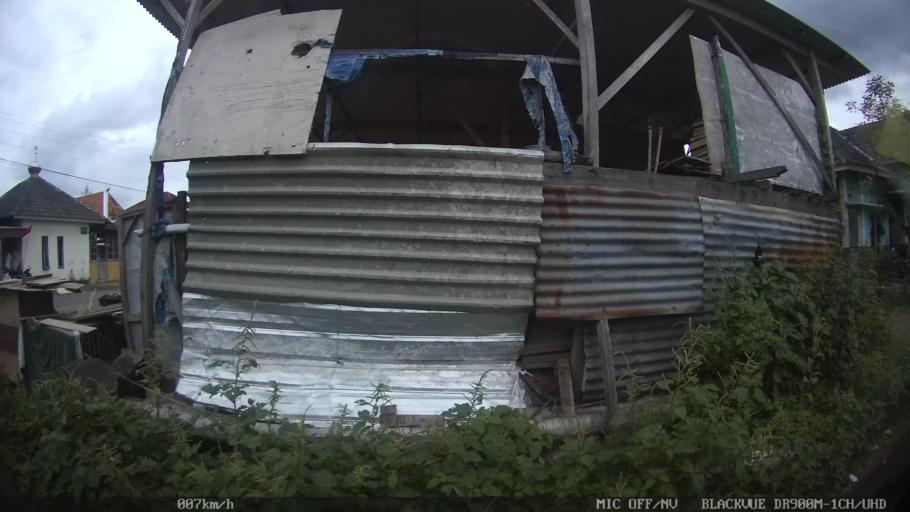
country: ID
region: Daerah Istimewa Yogyakarta
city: Sewon
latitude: -7.8504
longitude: 110.4171
